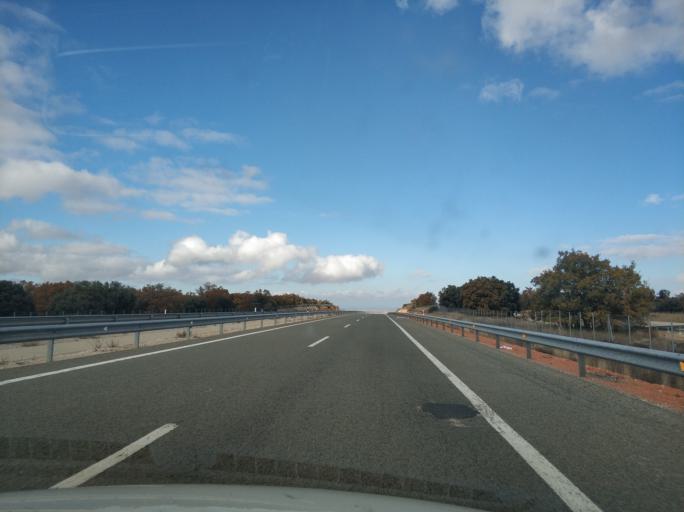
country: ES
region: Castille and Leon
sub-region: Provincia de Soria
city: Adradas
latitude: 41.3042
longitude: -2.4798
